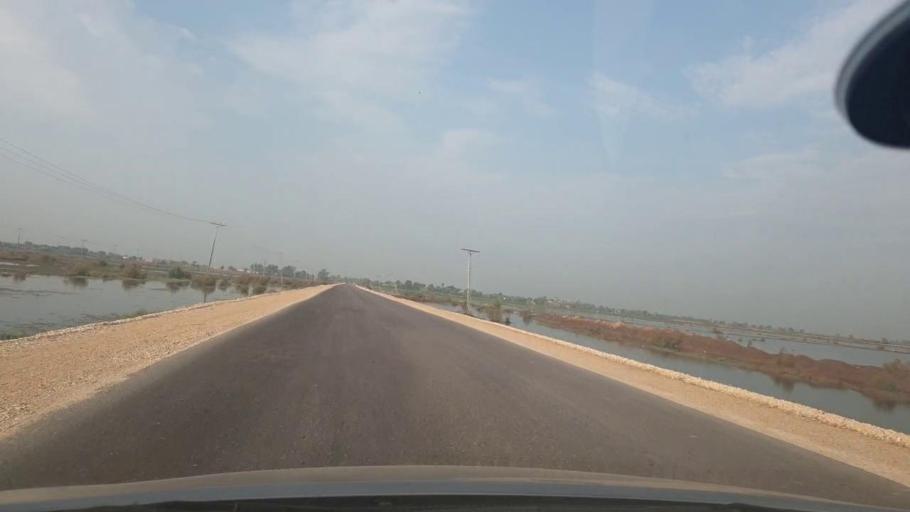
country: PK
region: Sindh
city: Jacobabad
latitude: 28.2225
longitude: 68.3754
